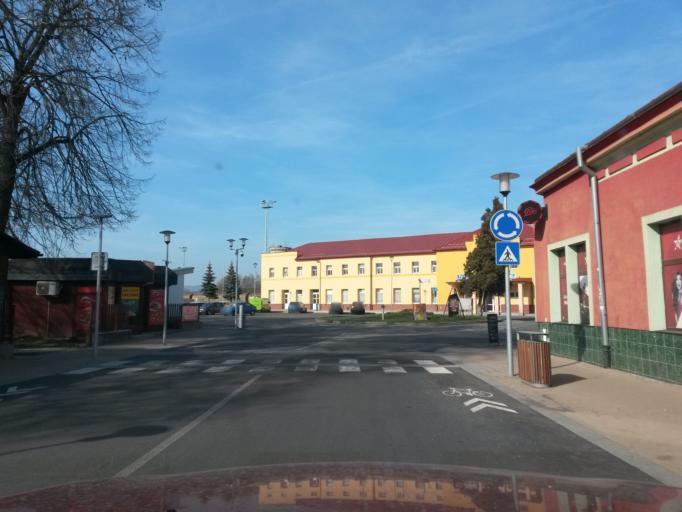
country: SK
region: Banskobystricky
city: Lucenec
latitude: 48.3352
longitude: 19.6671
